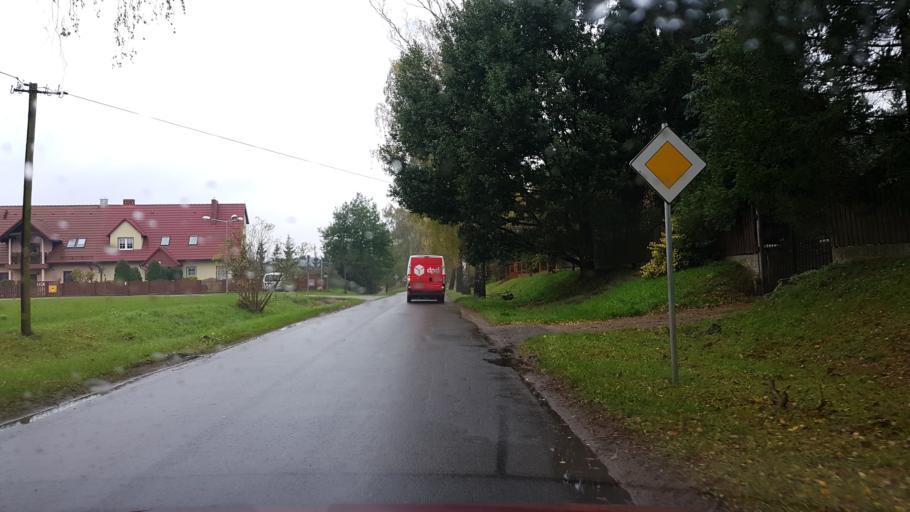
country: PL
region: Greater Poland Voivodeship
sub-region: Powiat zlotowski
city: Krajenka
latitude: 53.3040
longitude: 16.9848
